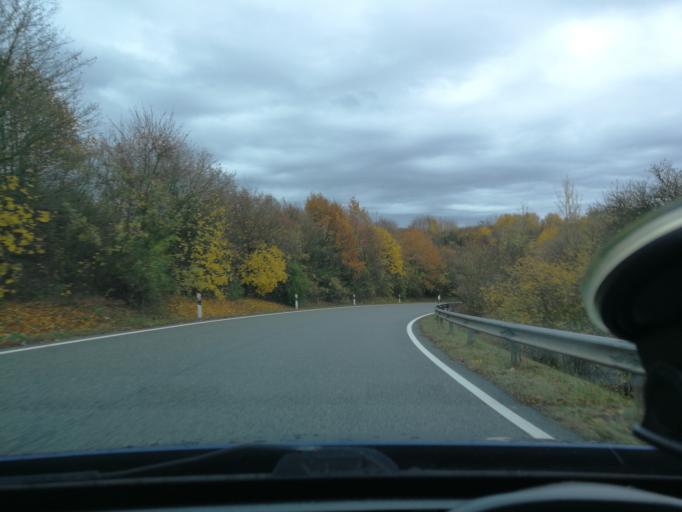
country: DE
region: Rheinland-Pfalz
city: Aach
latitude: 49.7726
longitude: 6.5983
